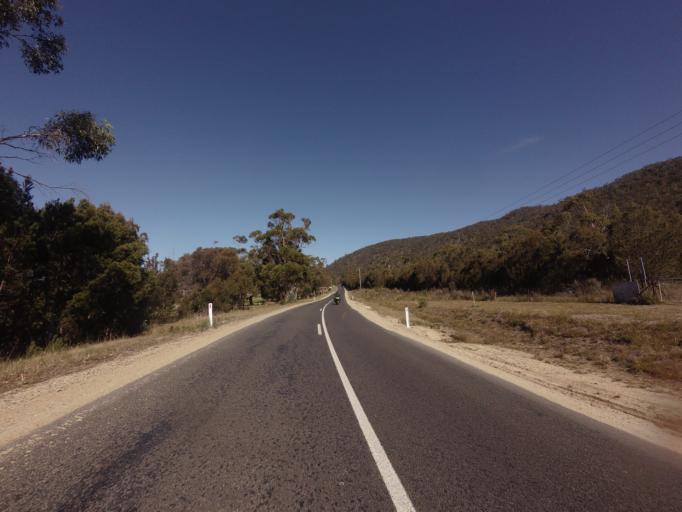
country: AU
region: Tasmania
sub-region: Break O'Day
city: St Helens
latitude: -41.8505
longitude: 148.2623
